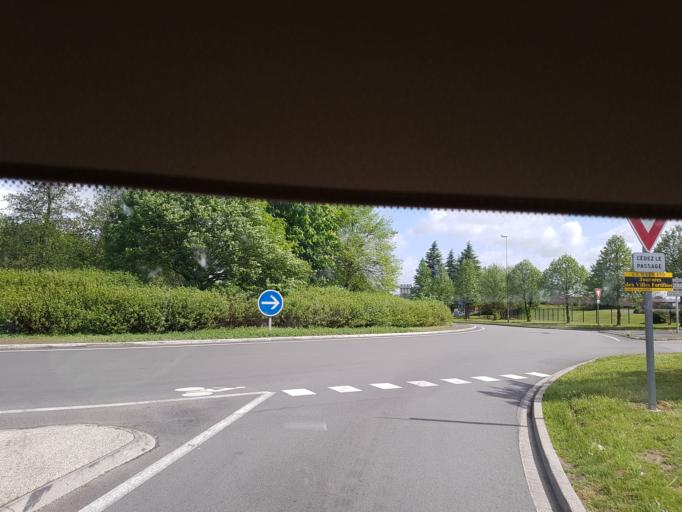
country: FR
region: Nord-Pas-de-Calais
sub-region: Departement du Nord
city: Proville
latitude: 50.1742
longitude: 3.1973
